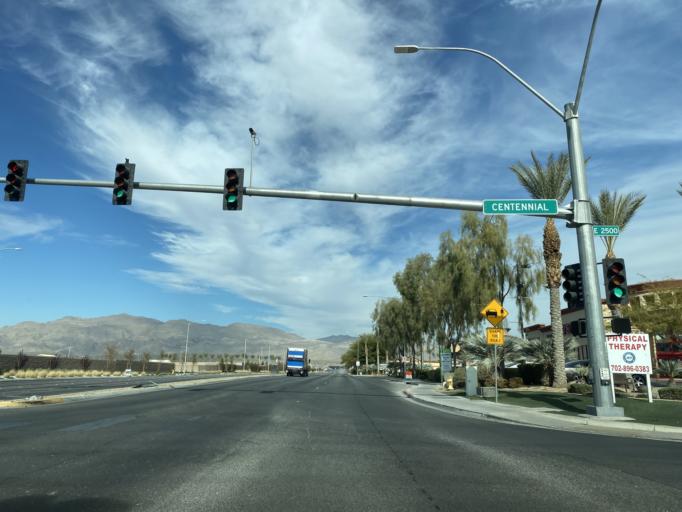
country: US
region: Nevada
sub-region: Clark County
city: Nellis Air Force Base
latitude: 36.2763
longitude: -115.1168
